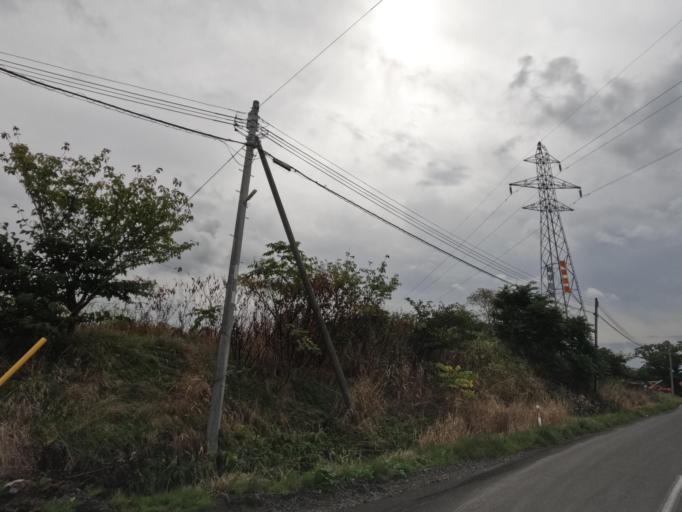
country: JP
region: Hokkaido
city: Date
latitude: 42.4546
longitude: 140.9067
